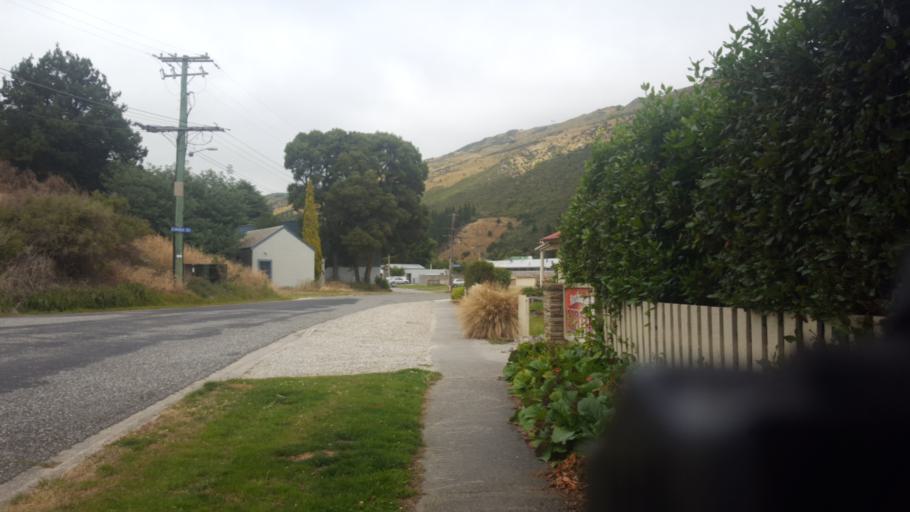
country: NZ
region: Otago
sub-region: Queenstown-Lakes District
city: Kingston
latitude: -45.5428
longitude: 169.3164
